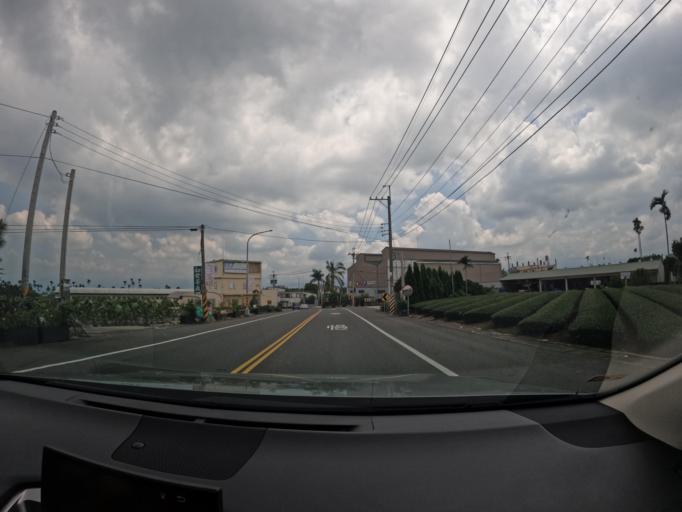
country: TW
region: Taiwan
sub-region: Nantou
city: Nantou
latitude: 23.8324
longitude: 120.6427
